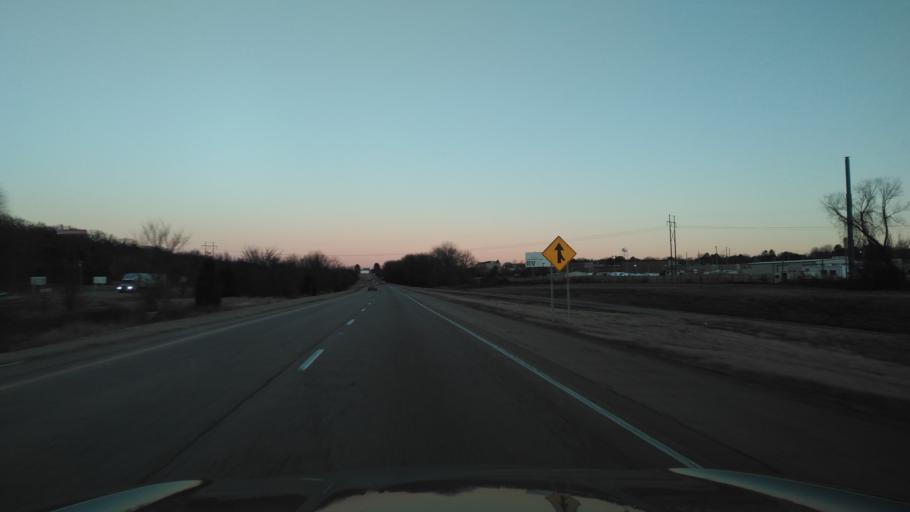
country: US
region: Arkansas
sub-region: Crawford County
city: Van Buren
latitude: 35.4624
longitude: -94.3556
